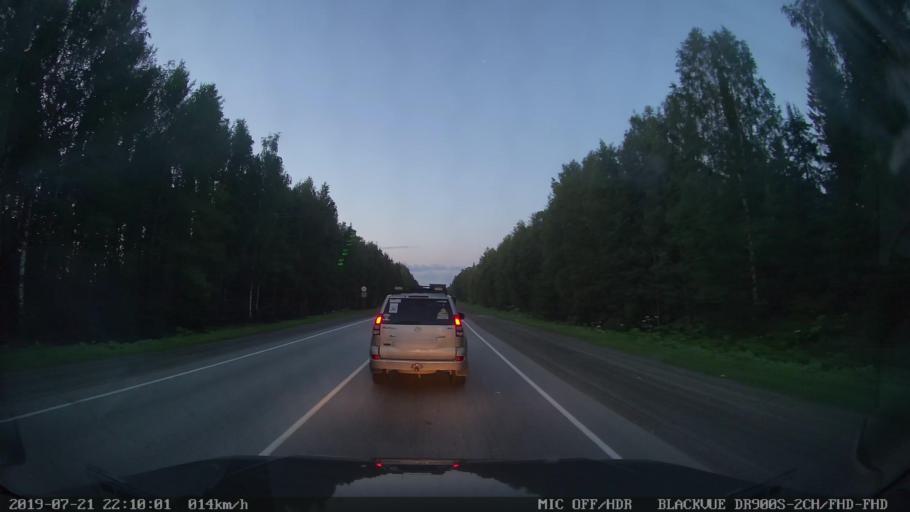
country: RU
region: Perm
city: Chaykovskaya
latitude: 58.0158
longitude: 55.5255
